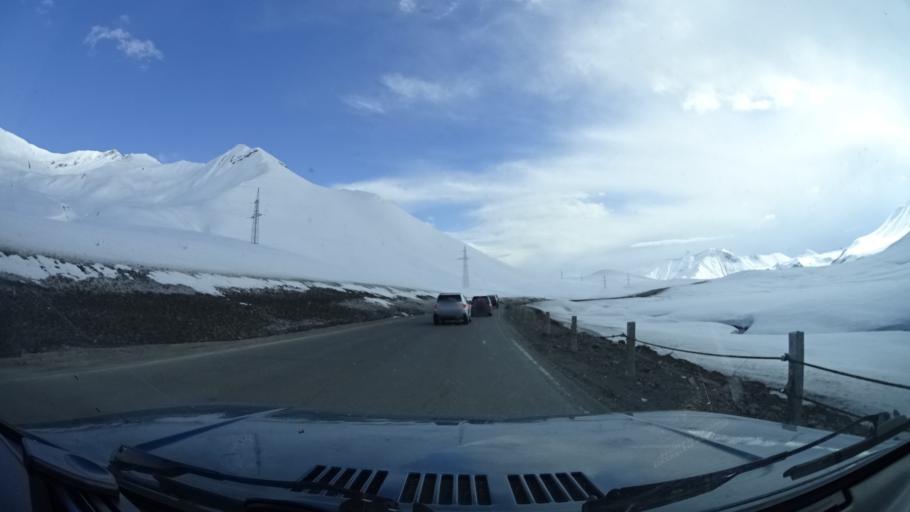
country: GE
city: Gudauri
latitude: 42.5131
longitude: 44.4624
